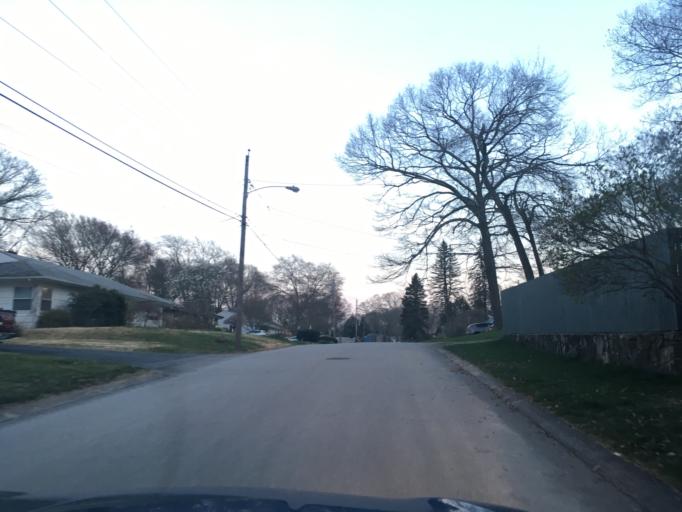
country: US
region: Rhode Island
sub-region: Kent County
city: East Greenwich
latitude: 41.6244
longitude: -71.4881
